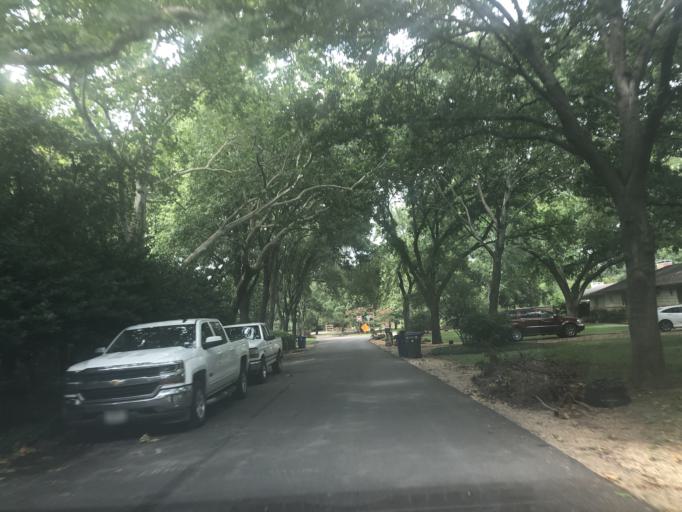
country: US
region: Texas
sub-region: Dallas County
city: University Park
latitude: 32.8560
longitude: -96.8358
